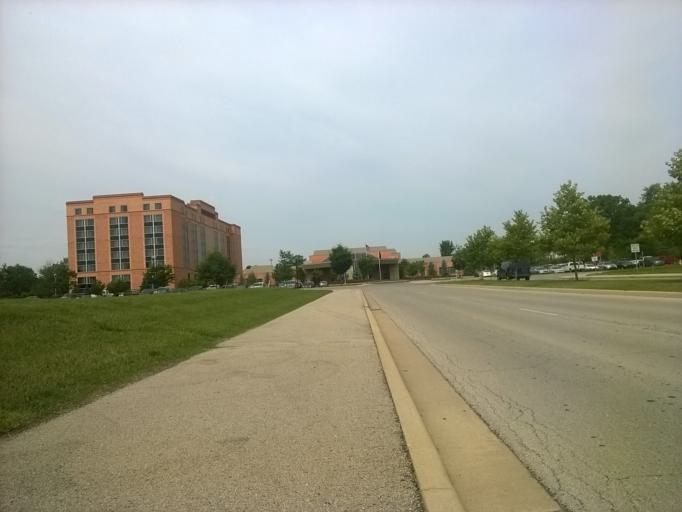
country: US
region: Indiana
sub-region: Hamilton County
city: Carmel
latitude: 39.9647
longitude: -86.1543
